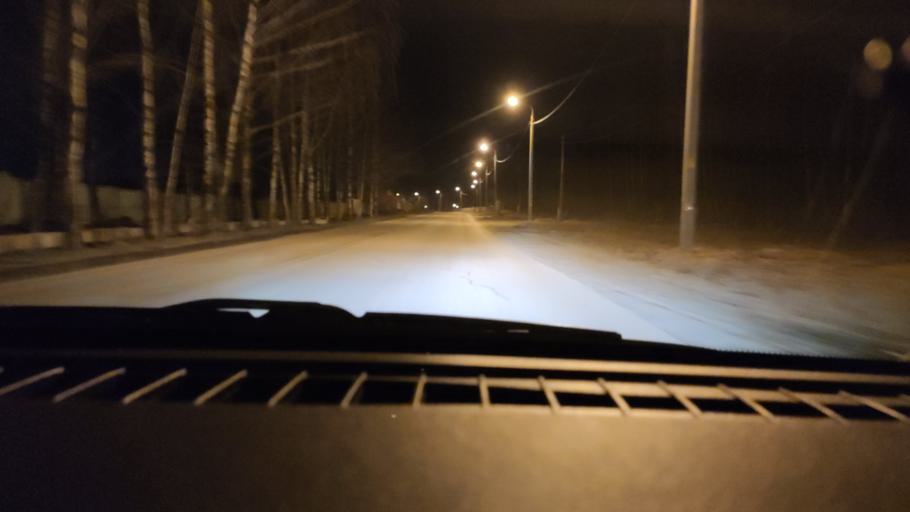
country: RU
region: Perm
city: Perm
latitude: 58.0412
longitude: 56.2695
